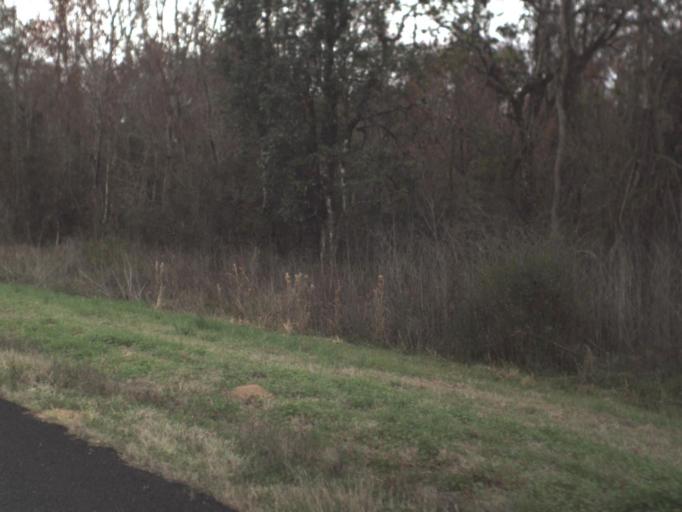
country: US
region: Florida
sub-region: Jefferson County
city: Monticello
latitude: 30.3836
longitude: -83.8274
